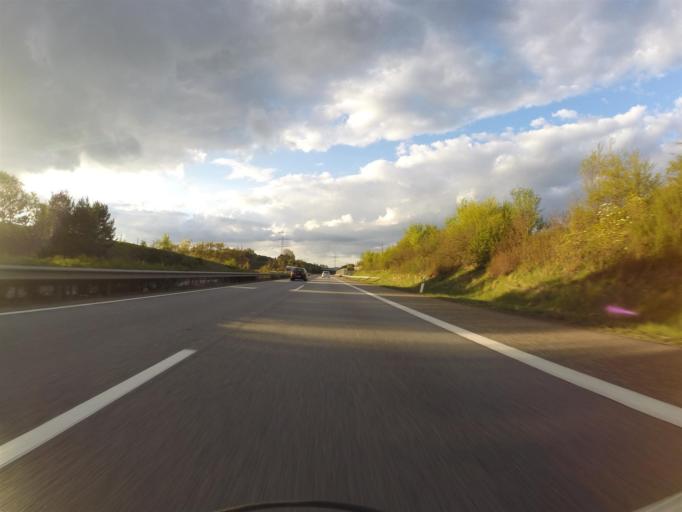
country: DE
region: Rheinland-Pfalz
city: Sembach
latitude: 49.5221
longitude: 7.8459
